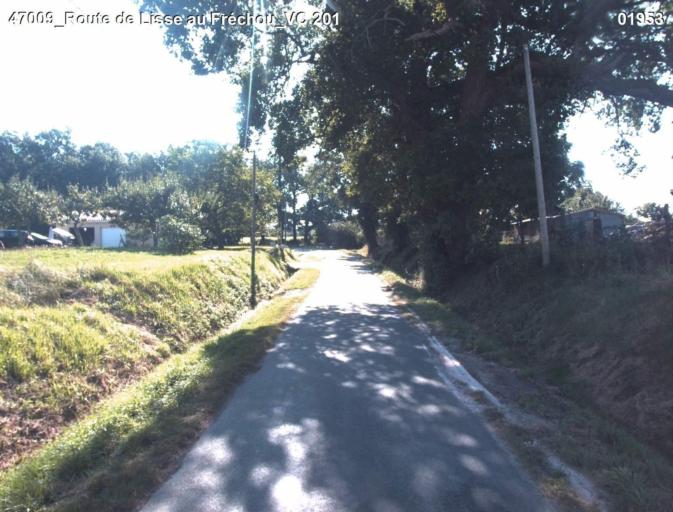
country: FR
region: Aquitaine
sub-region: Departement du Lot-et-Garonne
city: Mezin
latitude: 44.0940
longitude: 0.2884
